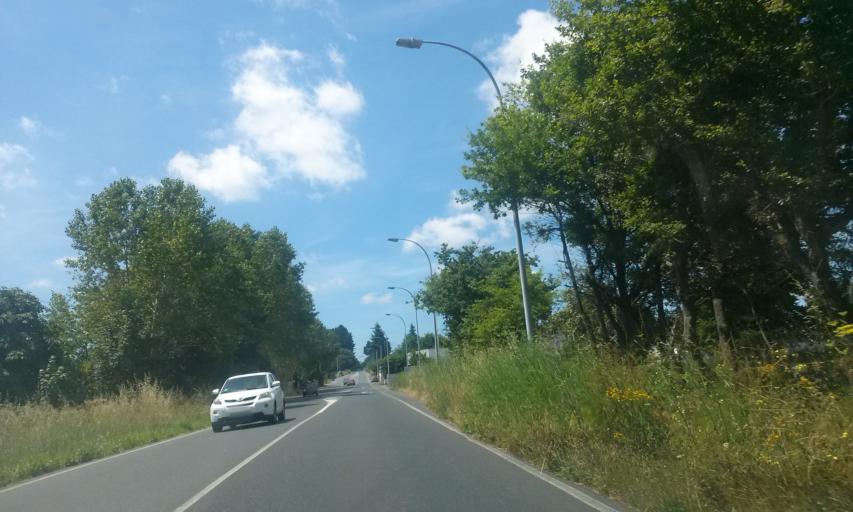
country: ES
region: Galicia
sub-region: Provincia de Lugo
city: Lugo
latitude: 42.9901
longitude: -7.5782
